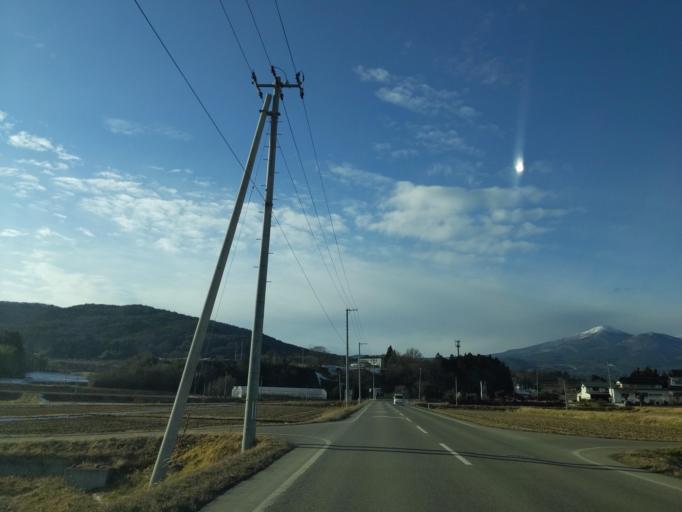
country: JP
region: Fukushima
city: Motomiya
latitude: 37.5276
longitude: 140.3647
